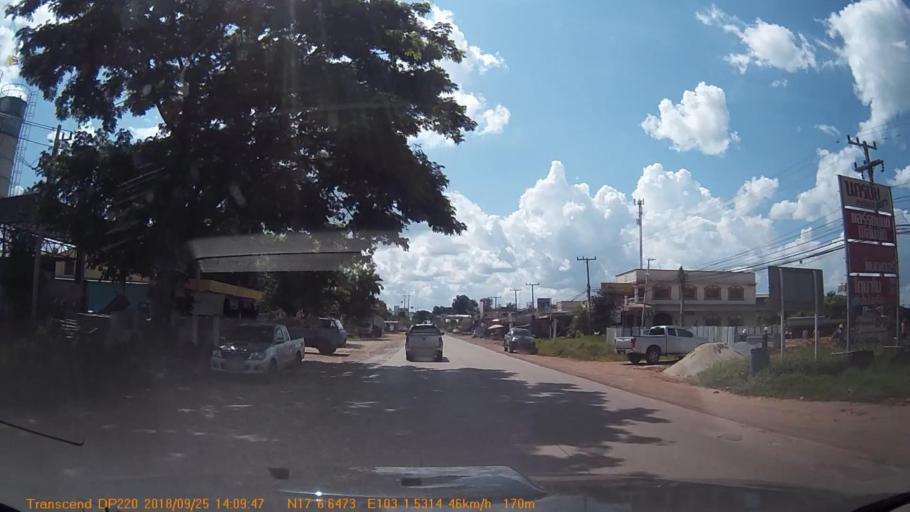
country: TH
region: Changwat Udon Thani
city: Kumphawapi
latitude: 17.1108
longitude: 103.0253
